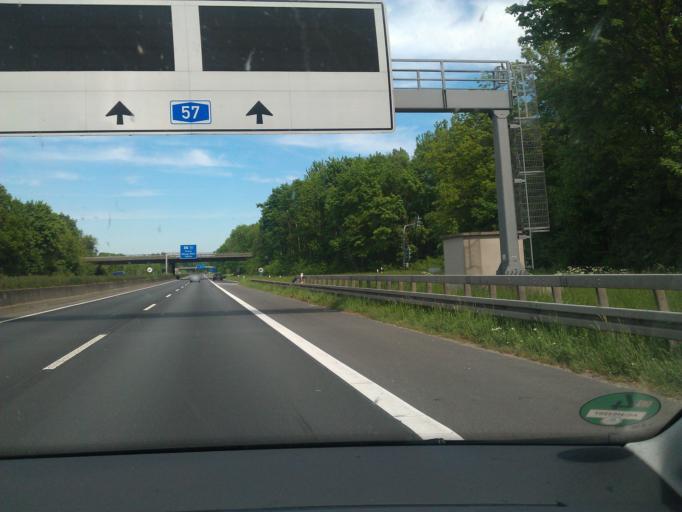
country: DE
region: North Rhine-Westphalia
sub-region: Regierungsbezirk Dusseldorf
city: Neubrueck
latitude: 51.1635
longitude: 6.6469
